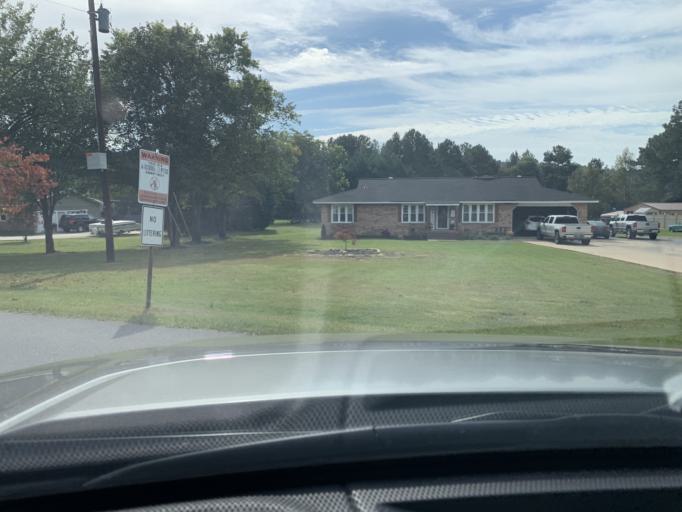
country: US
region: Georgia
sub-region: Polk County
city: Cedartown
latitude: 34.0581
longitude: -85.2622
